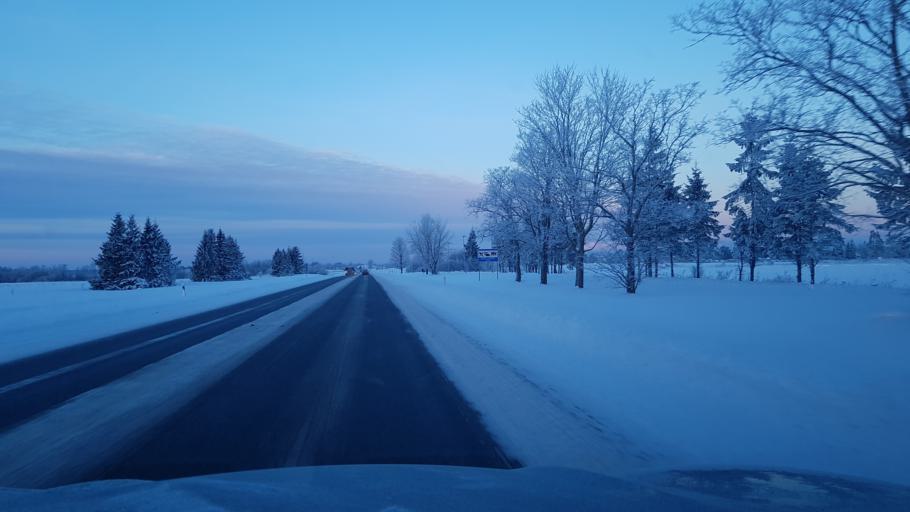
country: EE
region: Ida-Virumaa
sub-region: Narva linn
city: Narva
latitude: 59.3875
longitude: 28.1450
